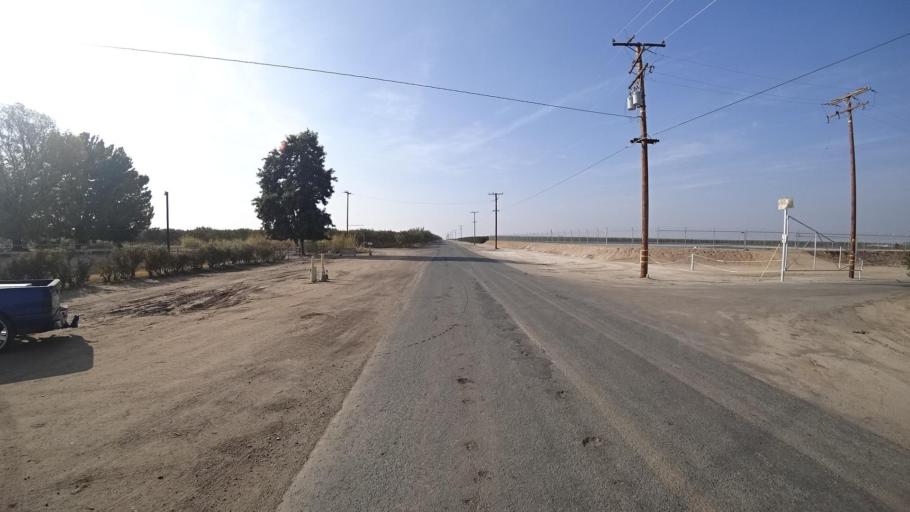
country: US
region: California
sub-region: Tulare County
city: Richgrove
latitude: 35.7908
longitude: -119.0799
